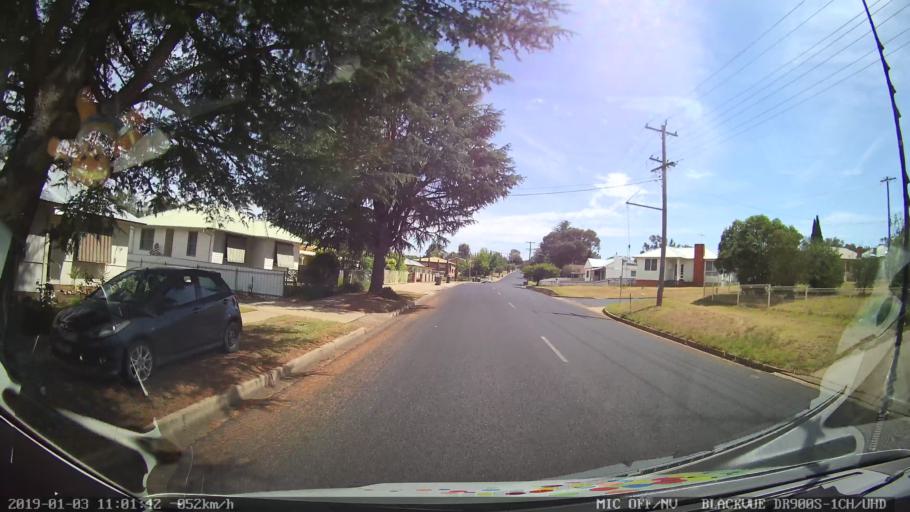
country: AU
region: New South Wales
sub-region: Young
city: Young
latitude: -34.3035
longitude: 148.2993
